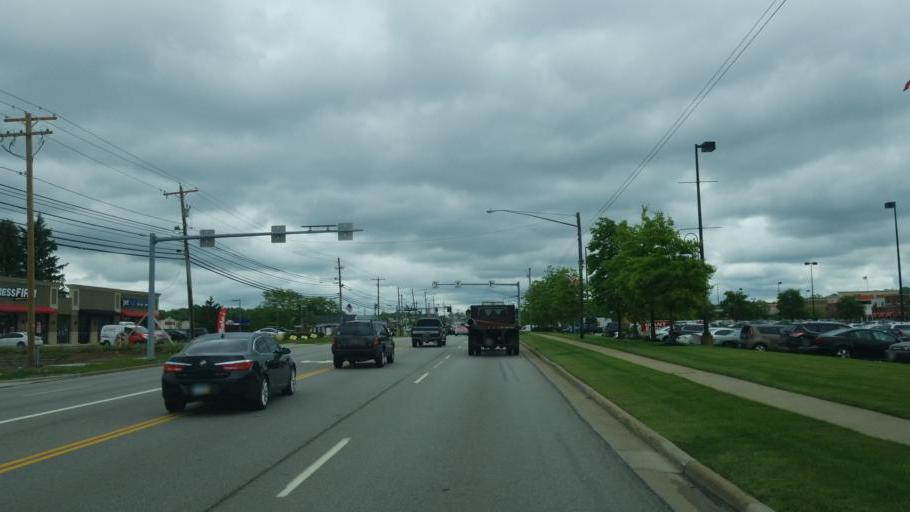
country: US
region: Ohio
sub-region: Medina County
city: Brunswick
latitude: 41.2382
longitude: -81.8103
